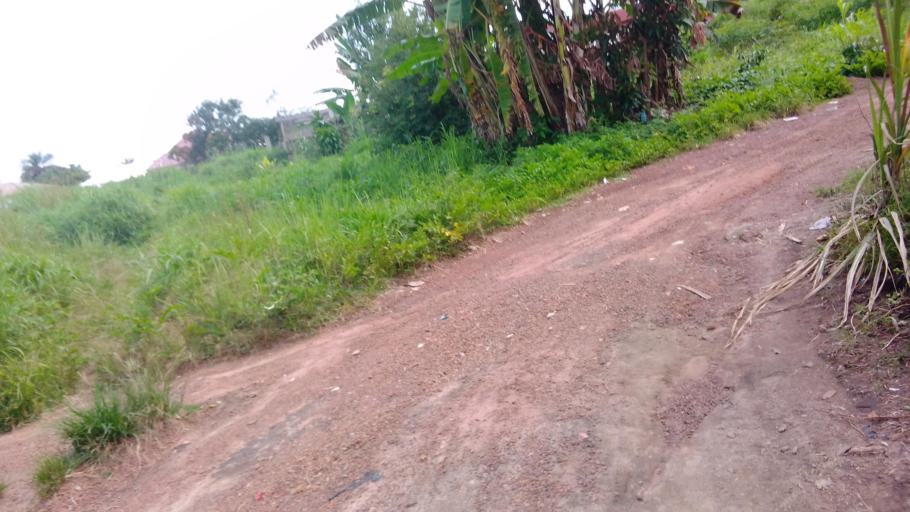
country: SL
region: Northern Province
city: Makeni
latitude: 8.8822
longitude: -12.0249
